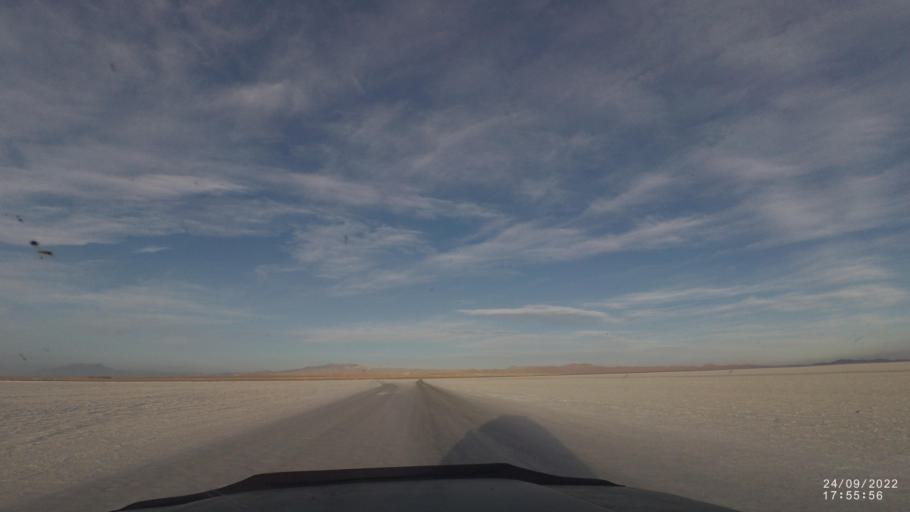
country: BO
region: Potosi
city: Colchani
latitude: -20.3257
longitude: -67.0222
